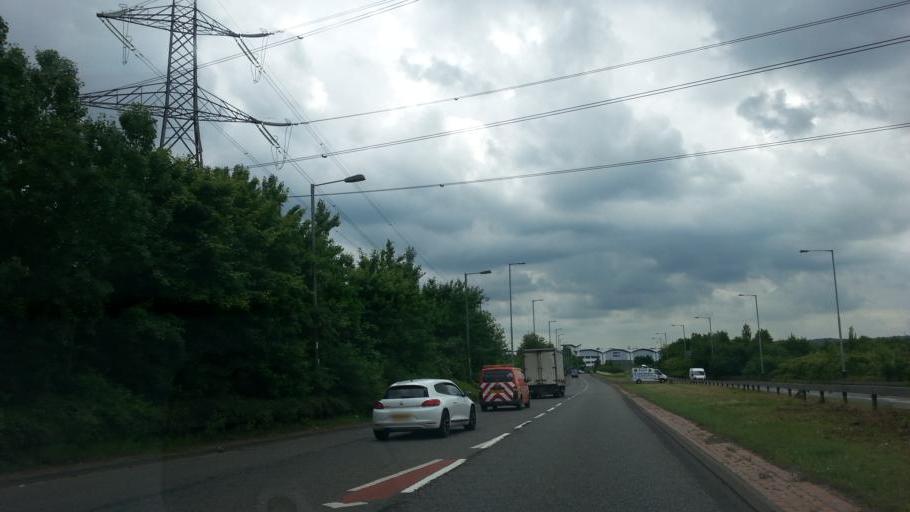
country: GB
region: England
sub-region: Walsall
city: Willenhall
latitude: 52.5734
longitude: -2.0496
